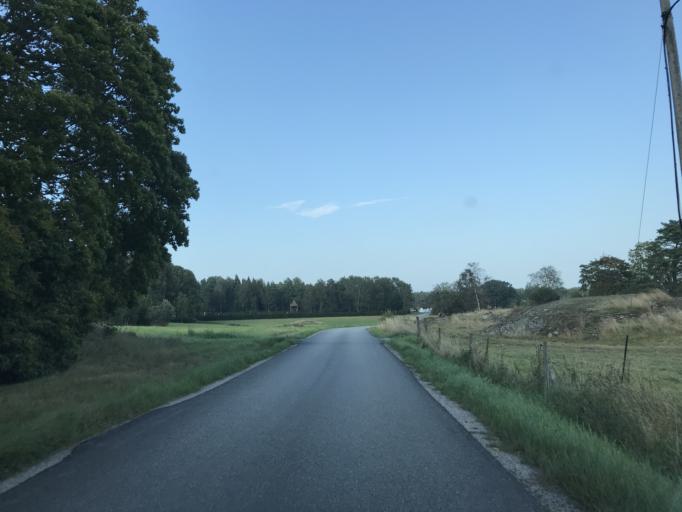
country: SE
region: Stockholm
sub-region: Norrtalje Kommun
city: Bjorko
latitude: 59.8520
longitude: 19.0136
